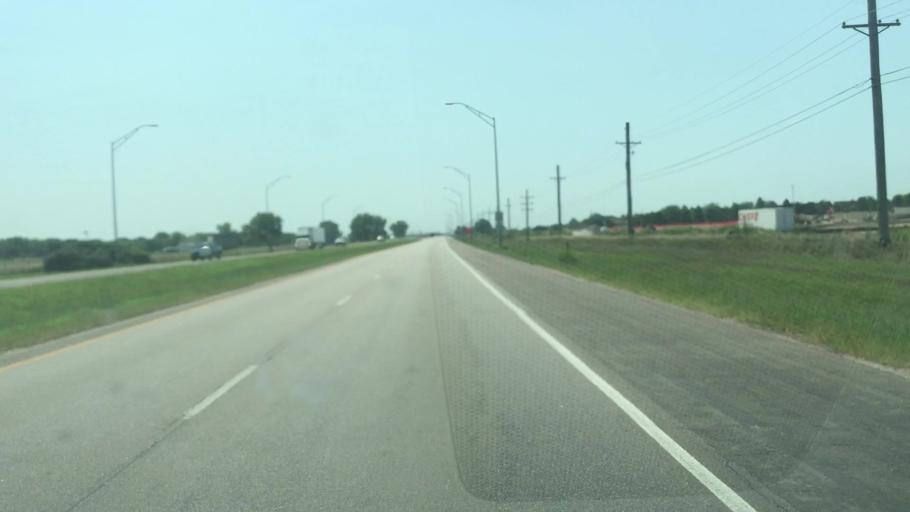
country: US
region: Nebraska
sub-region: Hall County
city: Grand Island
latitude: 40.8844
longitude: -98.3784
